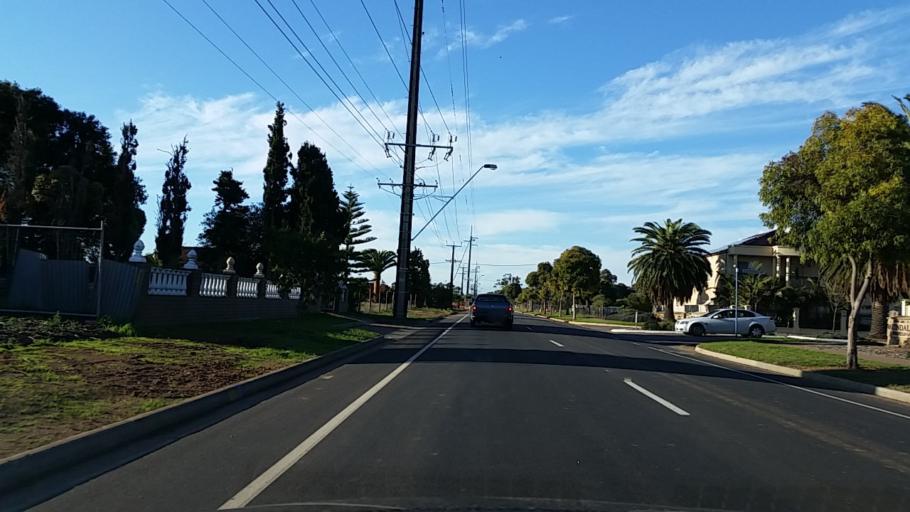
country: AU
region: South Australia
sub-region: Salisbury
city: Salisbury
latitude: -34.7868
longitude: 138.6037
